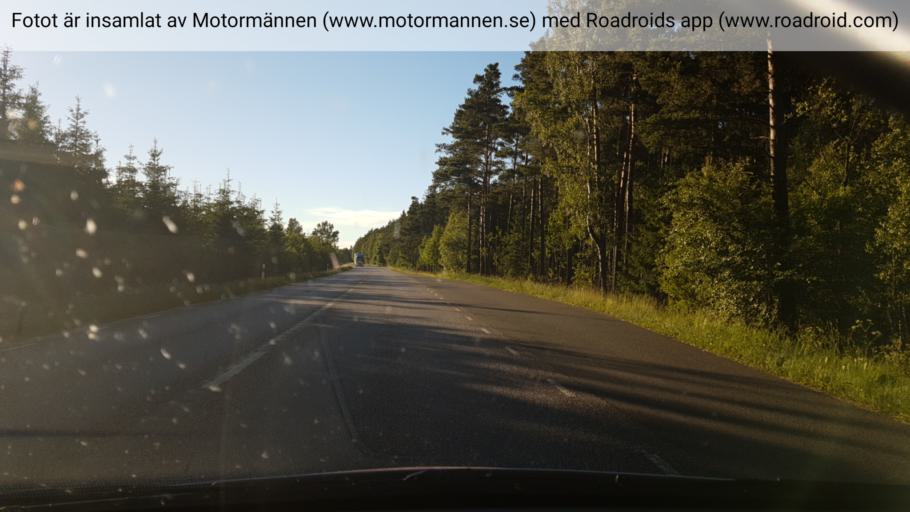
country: SE
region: Vaestra Goetaland
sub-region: Tidaholms Kommun
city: Tidaholm
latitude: 58.2003
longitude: 13.8875
